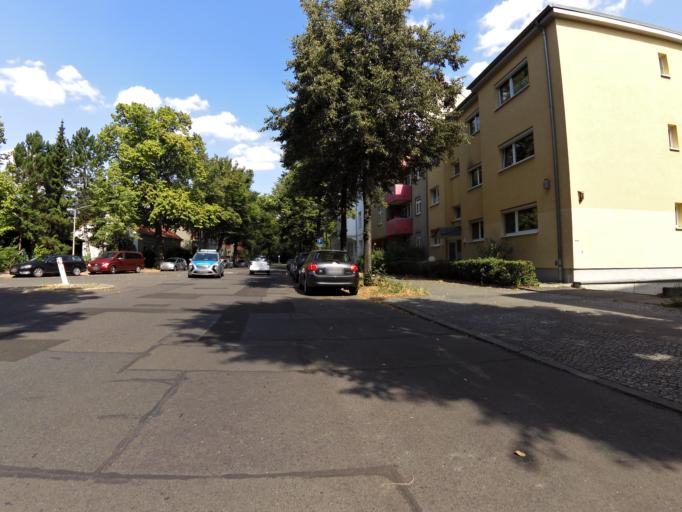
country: DE
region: Berlin
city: Lankwitz
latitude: 52.4376
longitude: 13.3534
